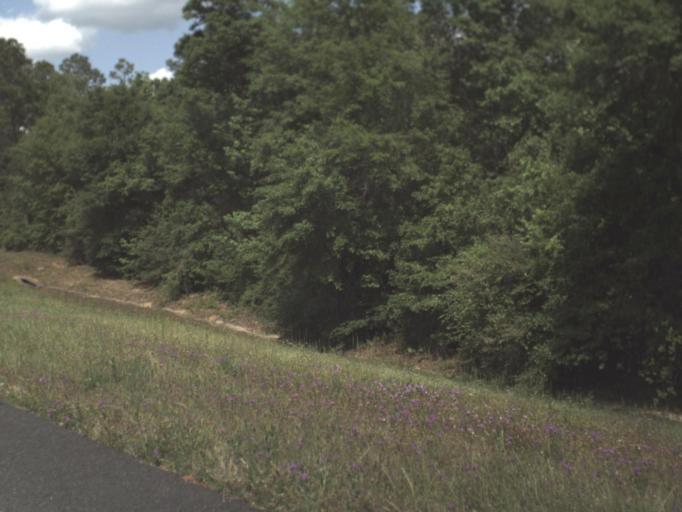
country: US
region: Florida
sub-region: Escambia County
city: Century
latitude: 30.8973
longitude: -87.3203
